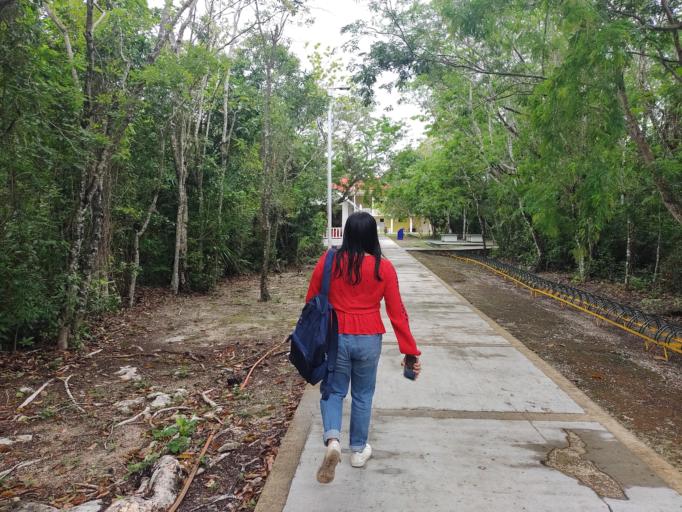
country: MX
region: Quintana Roo
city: San Miguel de Cozumel
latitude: 20.4887
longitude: -86.9409
